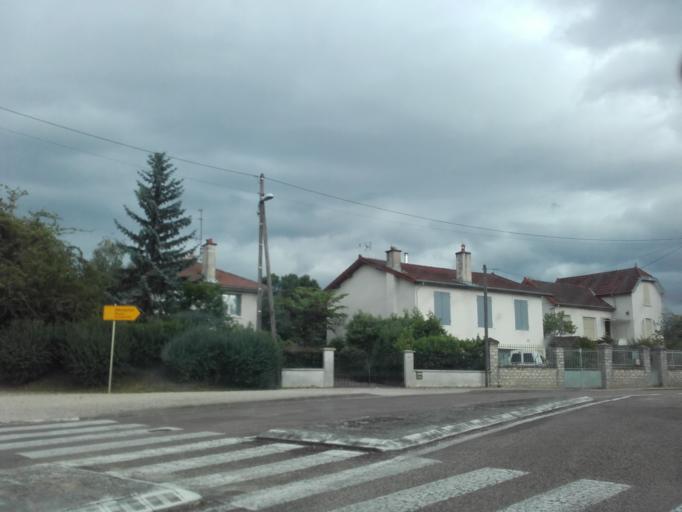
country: FR
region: Bourgogne
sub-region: Departement de Saone-et-Loire
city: Chagny
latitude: 46.9098
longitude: 4.7574
